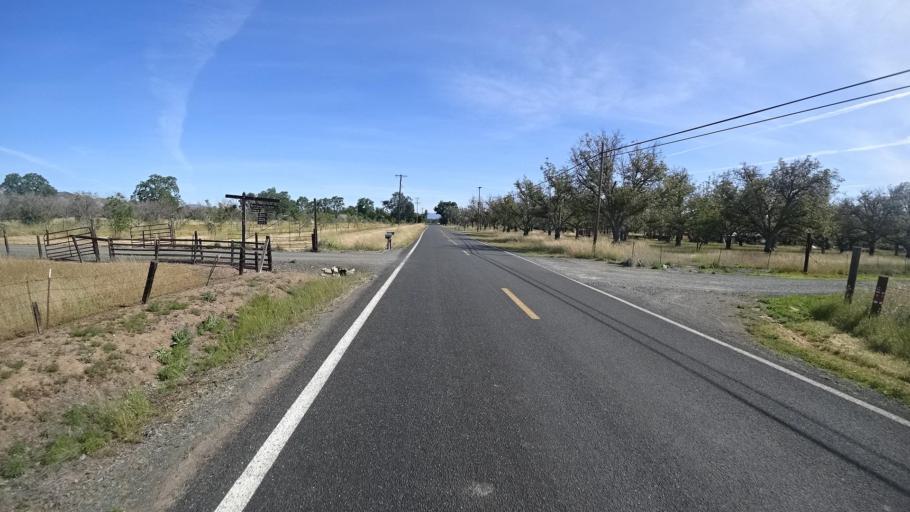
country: US
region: California
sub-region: Lake County
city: Kelseyville
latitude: 38.9792
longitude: -122.8945
